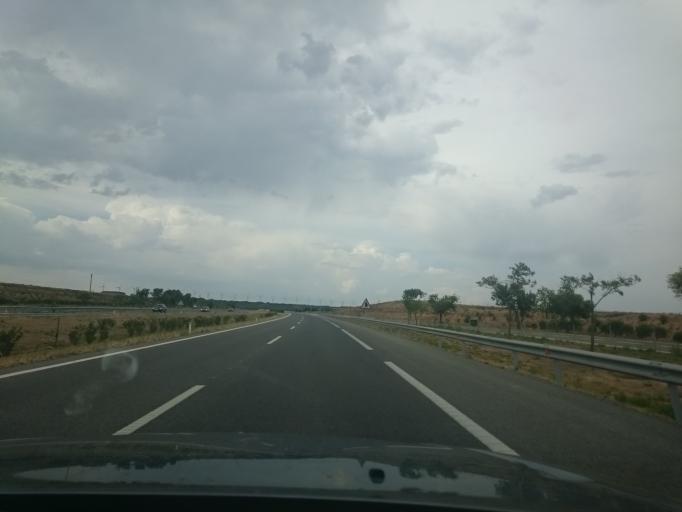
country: ES
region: Navarre
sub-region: Provincia de Navarra
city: Murchante
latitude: 42.0641
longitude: -1.6898
